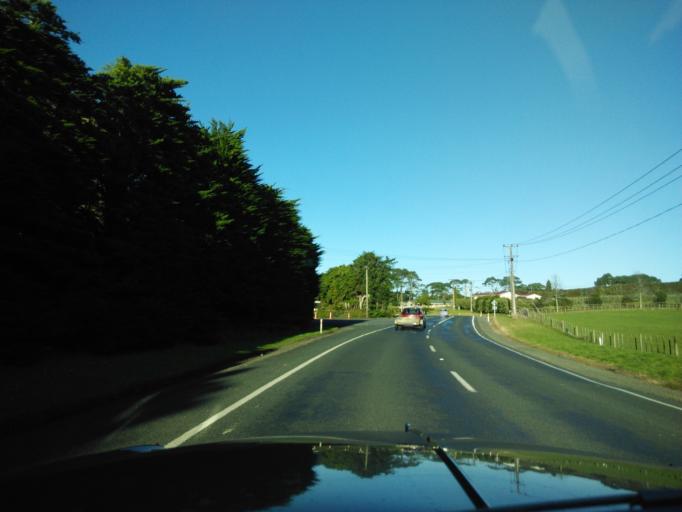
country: NZ
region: Auckland
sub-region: Auckland
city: Rothesay Bay
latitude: -36.7514
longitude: 174.6039
